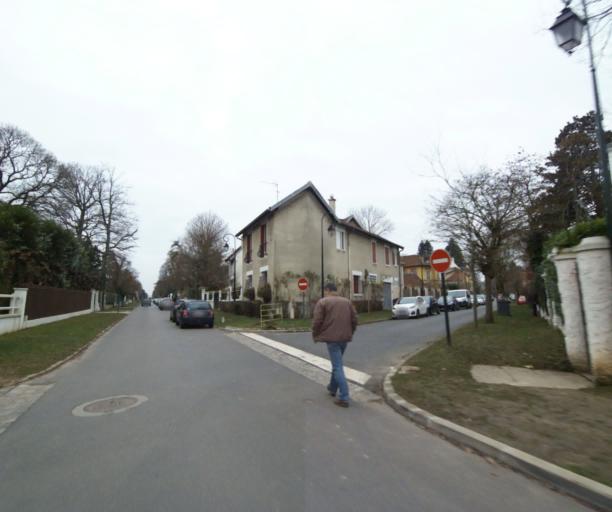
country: FR
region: Ile-de-France
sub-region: Departement des Hauts-de-Seine
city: Vaucresson
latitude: 48.8437
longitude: 2.1503
